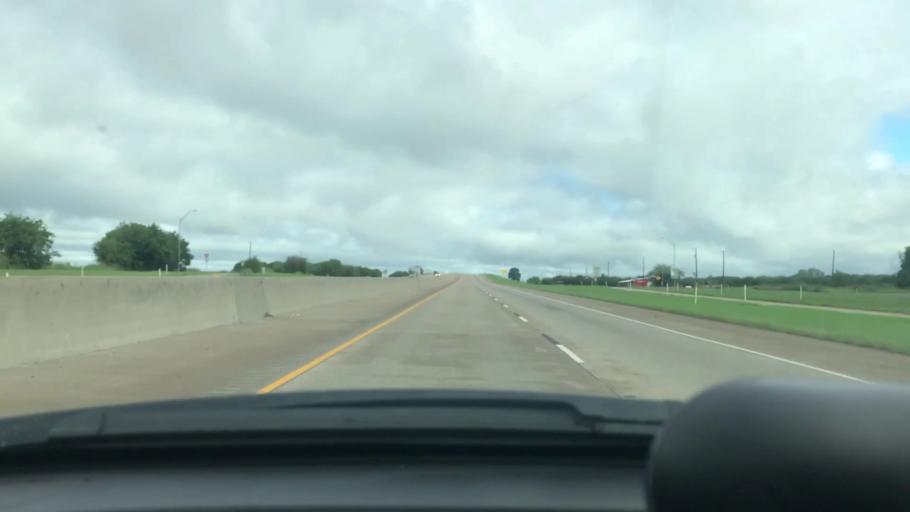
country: US
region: Texas
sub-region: Grayson County
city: Howe
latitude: 33.4604
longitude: -96.6101
